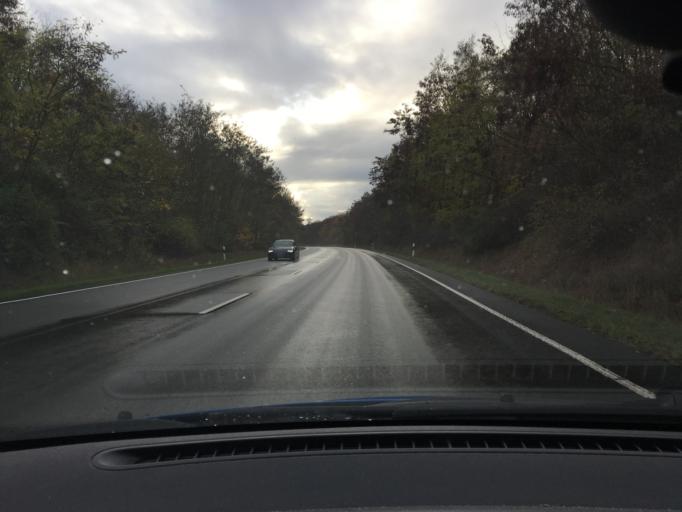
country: DE
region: Schleswig-Holstein
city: Molln
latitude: 53.6355
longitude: 10.6788
